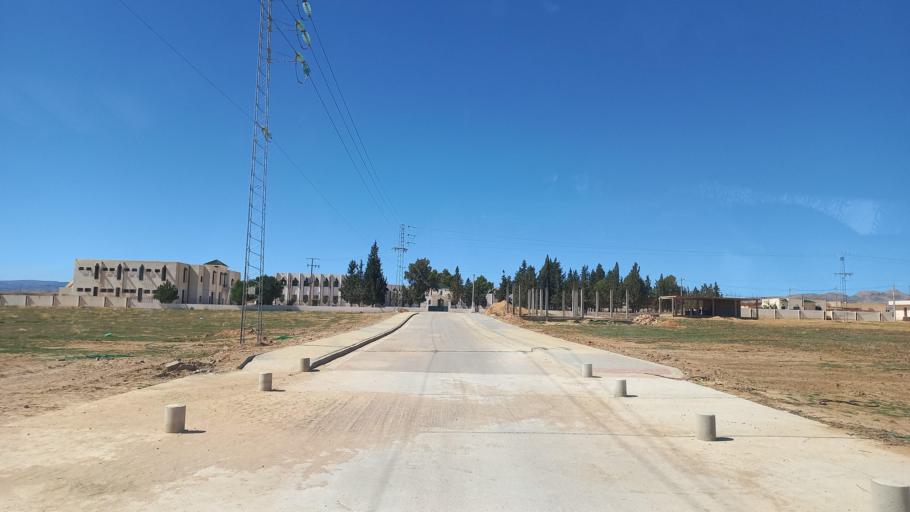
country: TN
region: Al Qasrayn
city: Sbiba
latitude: 35.3582
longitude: 9.0927
